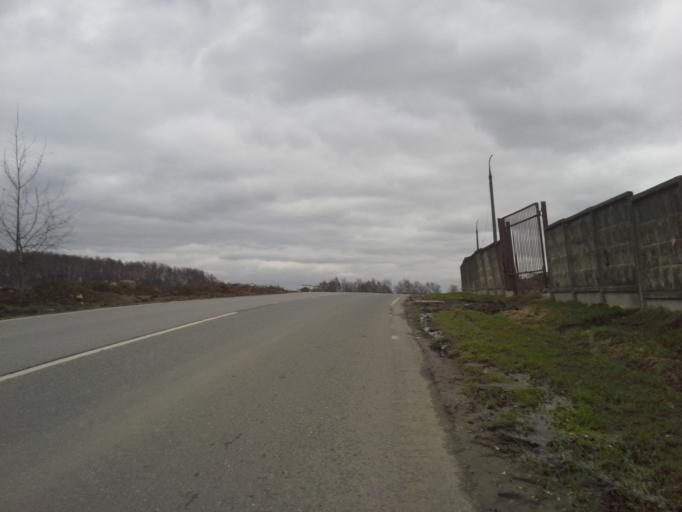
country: RU
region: Moskovskaya
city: Kommunarka
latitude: 55.5269
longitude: 37.4686
